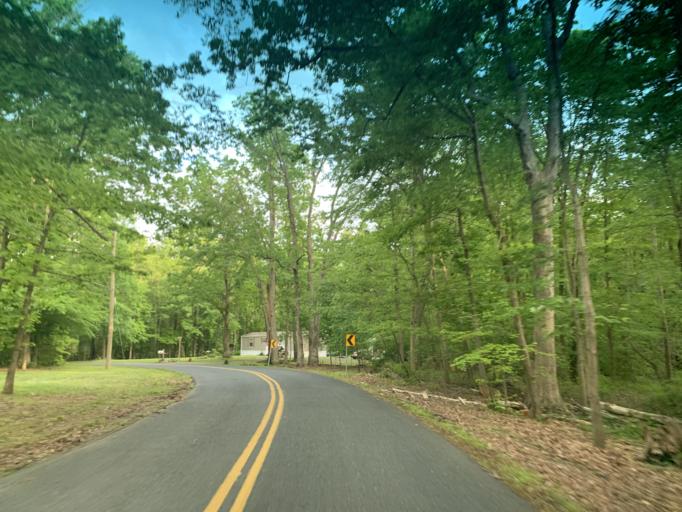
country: US
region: Pennsylvania
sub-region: York County
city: Susquehanna Trails
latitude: 39.6776
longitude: -76.2448
